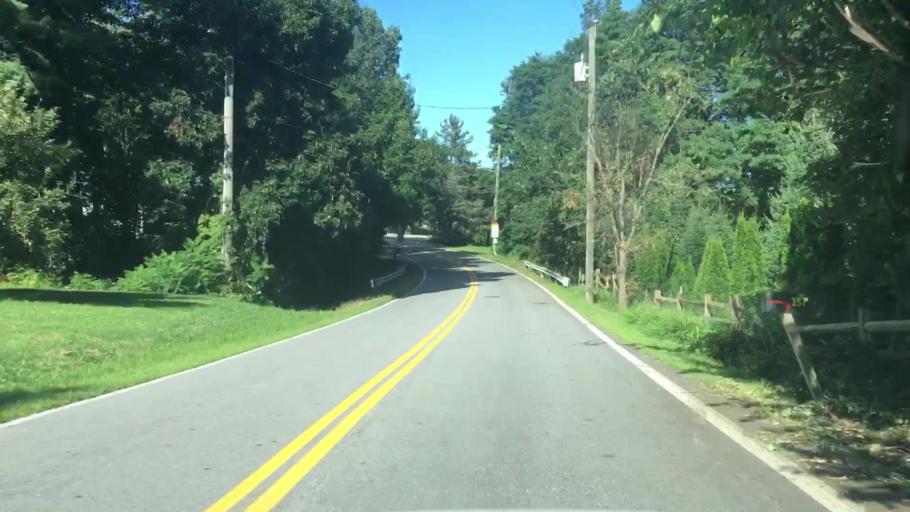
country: US
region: New Hampshire
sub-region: Strafford County
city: Dover
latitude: 43.1581
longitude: -70.8652
